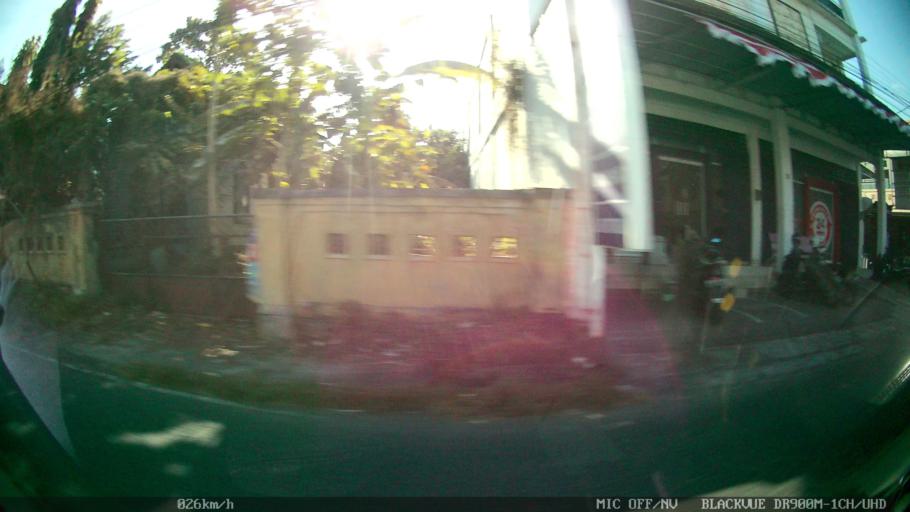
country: ID
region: Bali
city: Banjar Gunungpande
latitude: -8.6304
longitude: 115.1724
